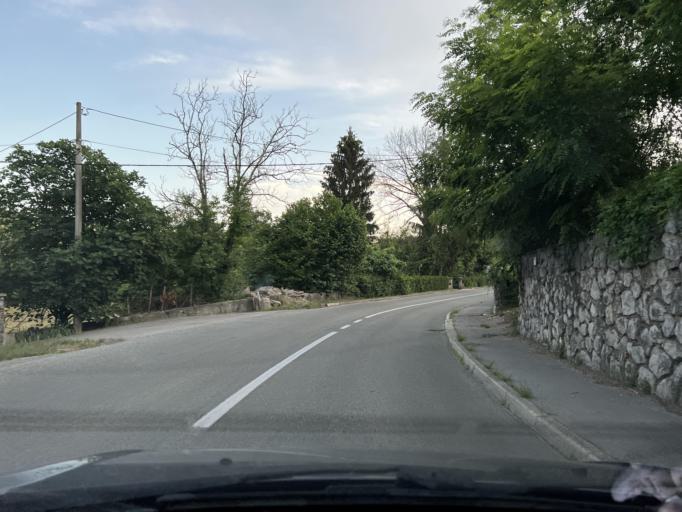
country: HR
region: Primorsko-Goranska
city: Drazice
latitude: 45.3853
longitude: 14.4487
